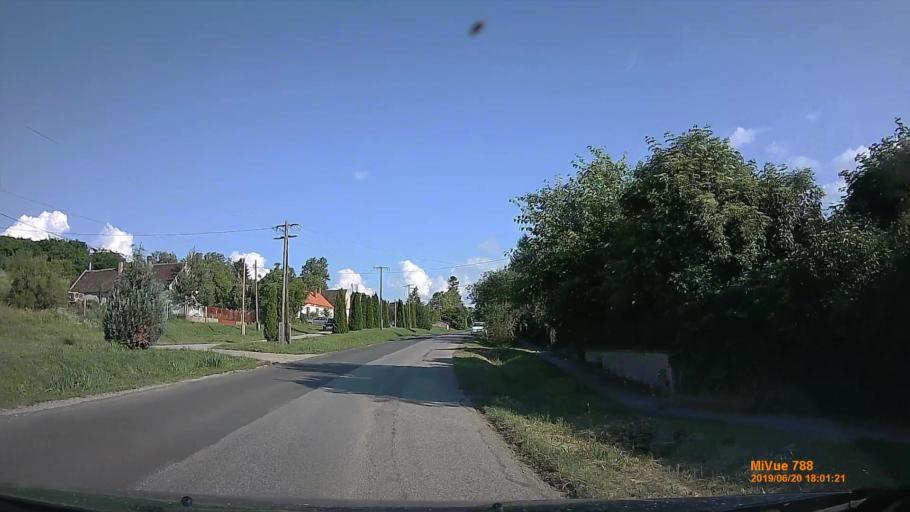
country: HU
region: Baranya
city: Buekkoesd
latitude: 46.0837
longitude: 17.9896
